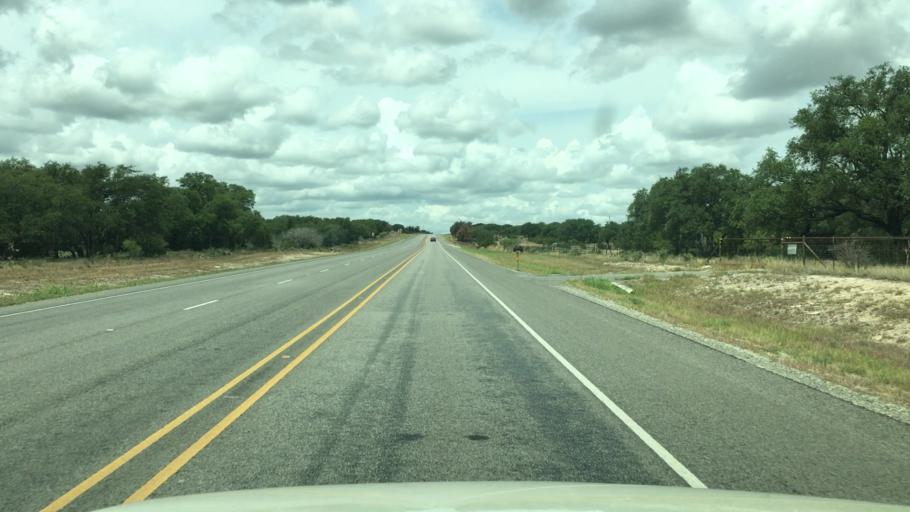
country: US
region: Texas
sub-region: McCulloch County
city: Brady
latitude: 31.0293
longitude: -99.2278
